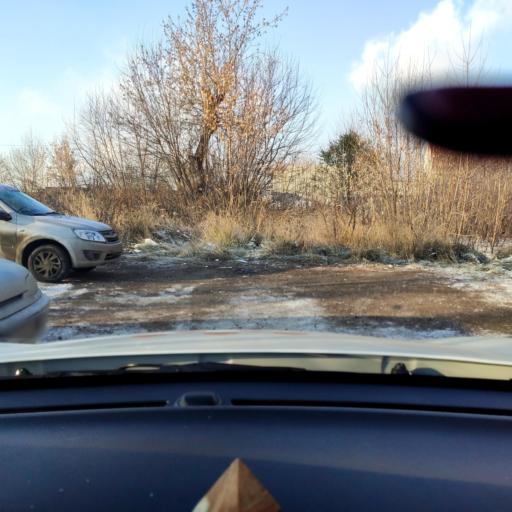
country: RU
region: Tatarstan
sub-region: Gorod Kazan'
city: Kazan
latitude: 55.8178
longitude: 49.0540
